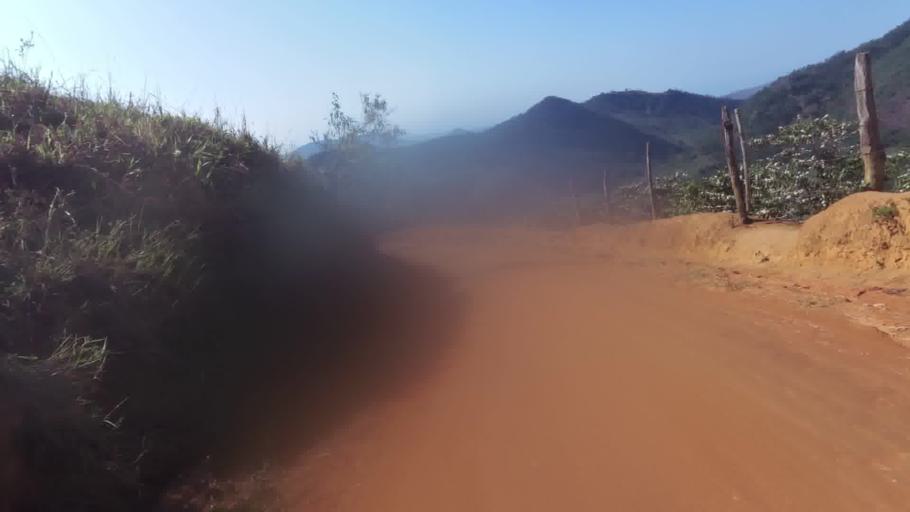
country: BR
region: Espirito Santo
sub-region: Alfredo Chaves
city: Alfredo Chaves
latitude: -20.6834
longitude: -40.7806
